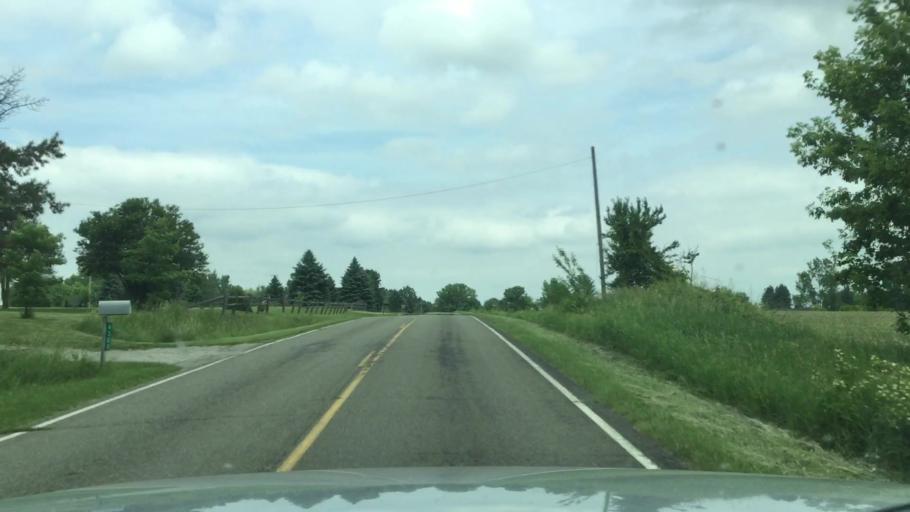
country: US
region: Michigan
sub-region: Shiawassee County
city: Durand
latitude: 42.9364
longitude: -83.9589
